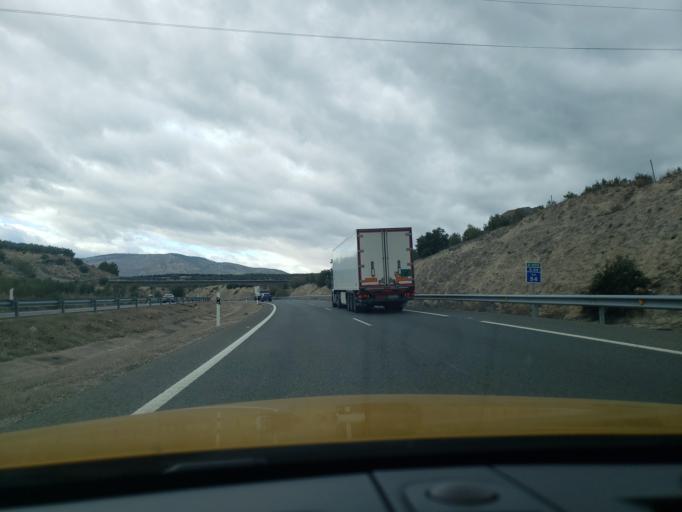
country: ES
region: Andalusia
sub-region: Provincia de Jaen
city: Pegalajar
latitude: 37.7181
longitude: -3.6497
